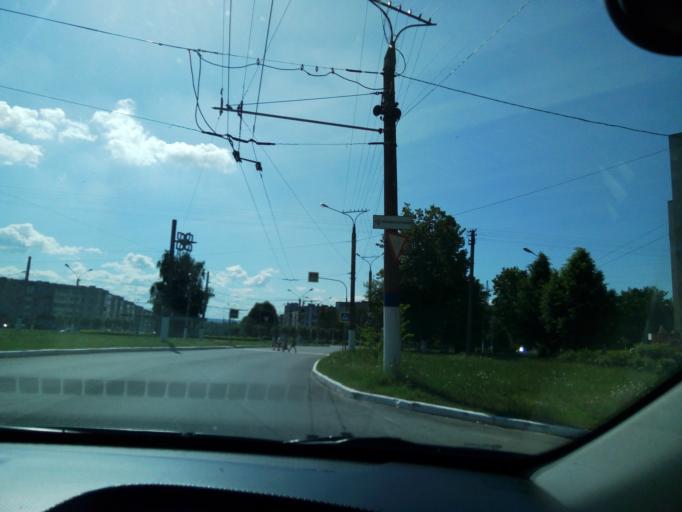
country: RU
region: Chuvashia
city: Novocheboksarsk
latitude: 56.1147
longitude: 47.4856
